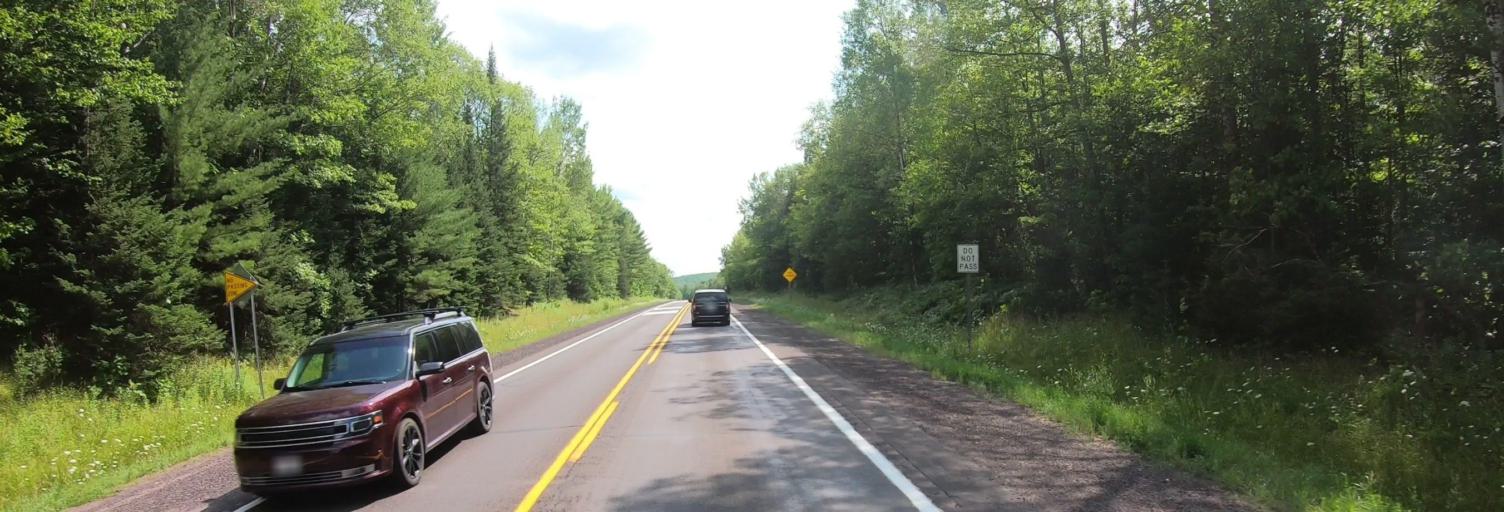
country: US
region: Michigan
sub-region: Ontonagon County
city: Ontonagon
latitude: 46.7739
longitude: -89.0732
